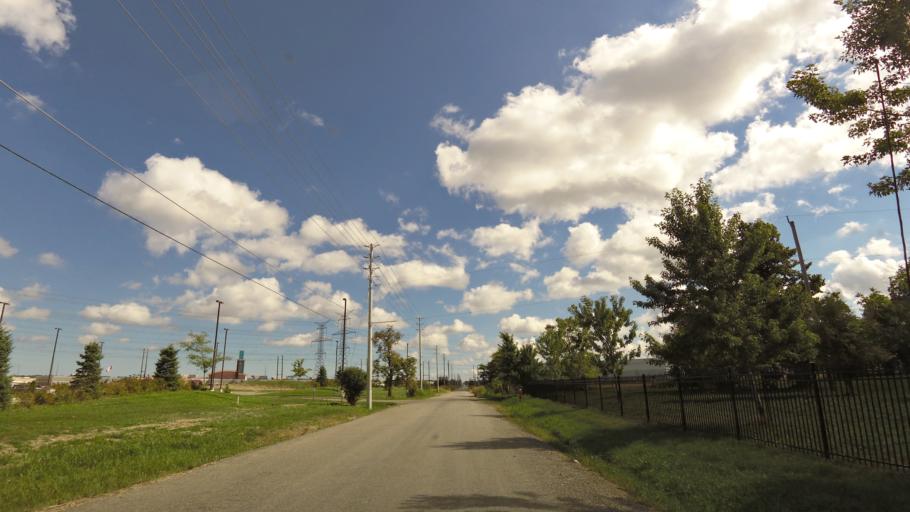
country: CA
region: Ontario
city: Brampton
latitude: 43.5978
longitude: -79.7956
